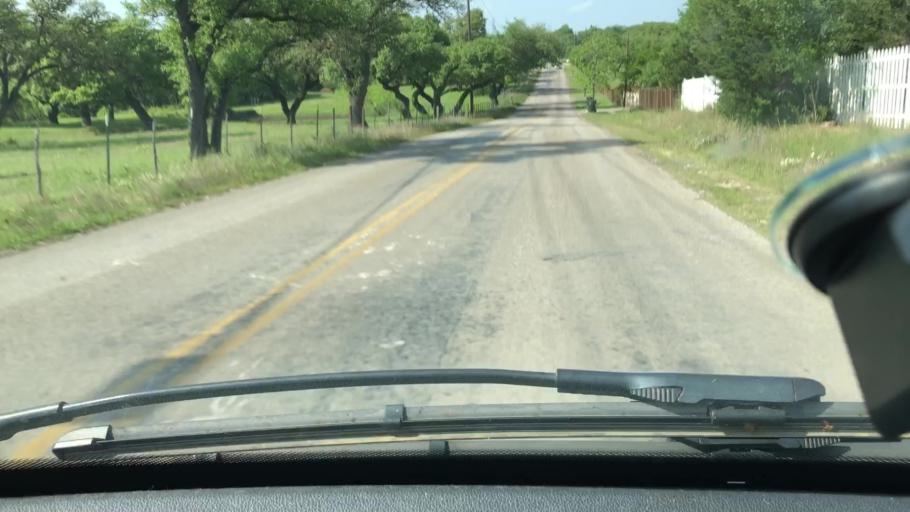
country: US
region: Texas
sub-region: Comal County
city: Bulverde
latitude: 29.7724
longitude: -98.4588
